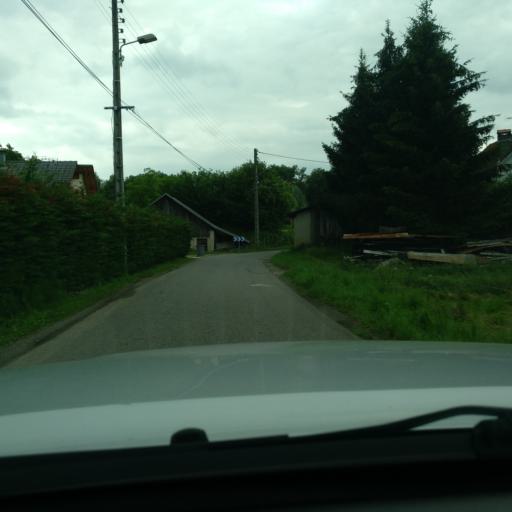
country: FR
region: Rhone-Alpes
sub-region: Departement de la Haute-Savoie
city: Amancy
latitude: 46.0799
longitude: 6.3496
